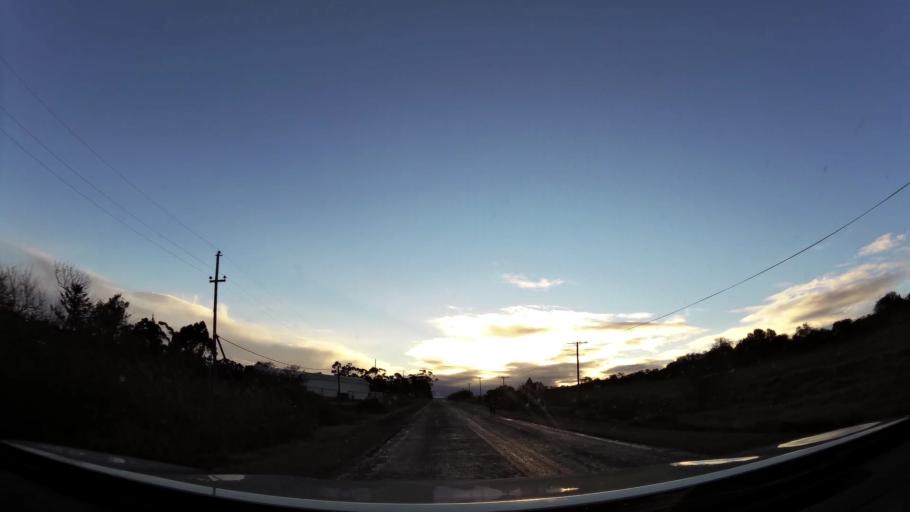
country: ZA
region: Western Cape
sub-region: Eden District Municipality
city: Riversdale
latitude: -34.0823
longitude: 20.9444
